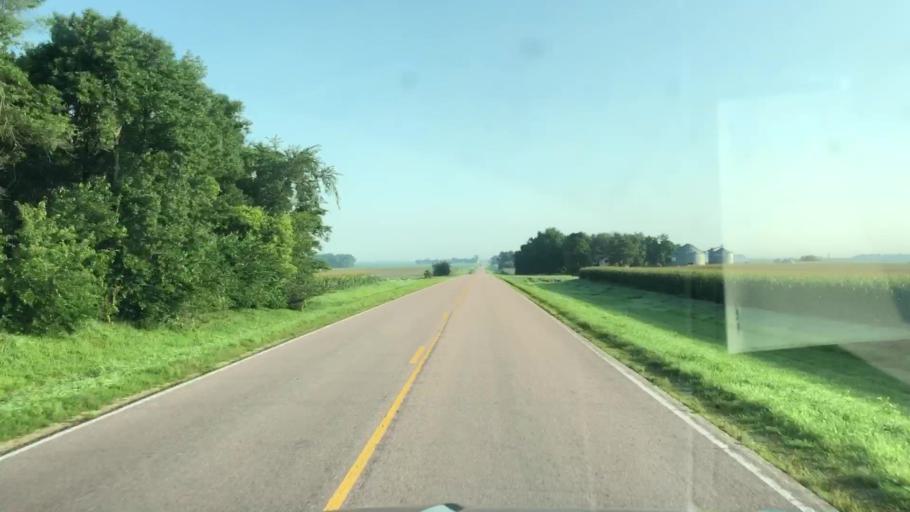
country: US
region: Iowa
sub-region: Lyon County
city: George
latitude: 43.2908
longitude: -95.9995
